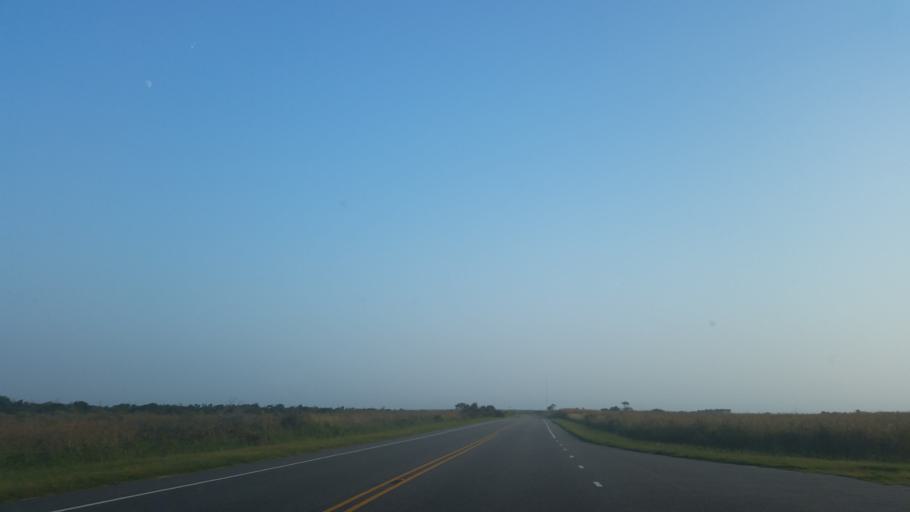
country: US
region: North Carolina
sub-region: Dare County
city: Wanchese
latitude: 35.8641
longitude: -75.5782
